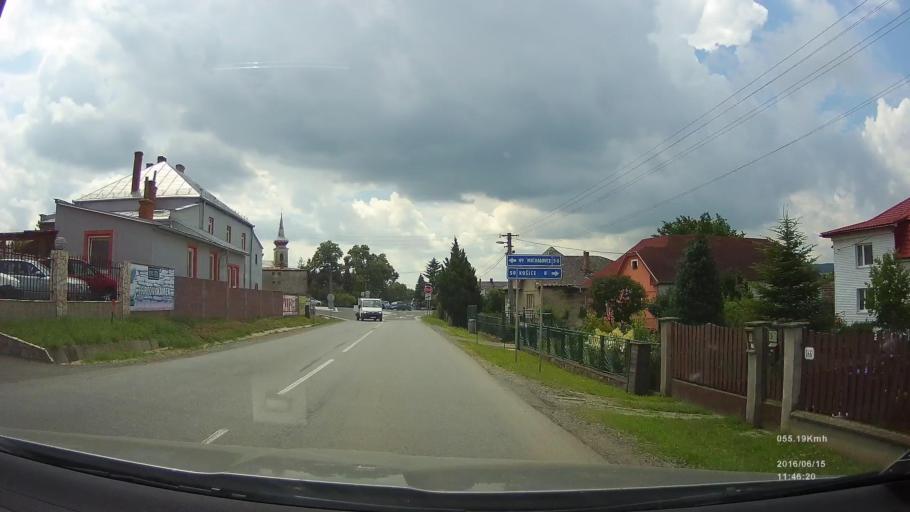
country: SK
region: Kosicky
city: Kosice
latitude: 48.7347
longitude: 21.3461
